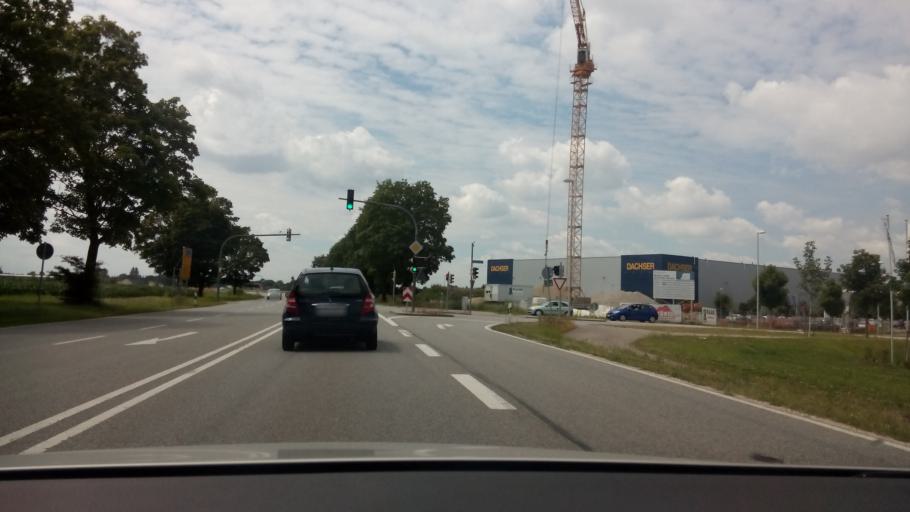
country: DE
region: Bavaria
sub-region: Upper Bavaria
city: Neufahrn bei Freising
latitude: 48.3300
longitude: 11.6952
